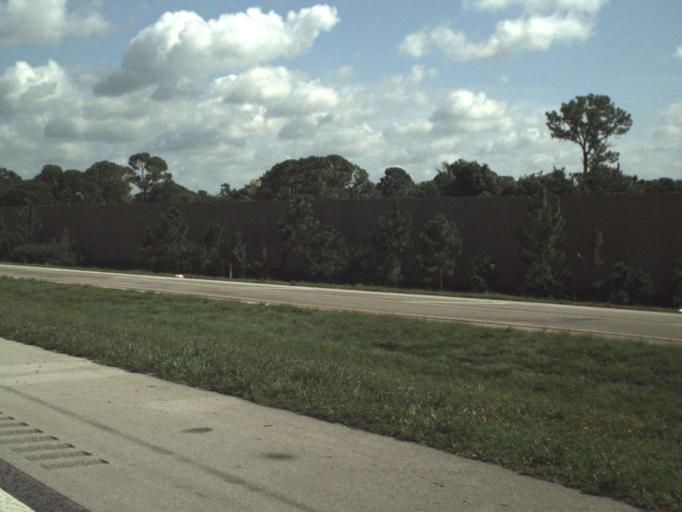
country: US
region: Florida
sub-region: Palm Beach County
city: Limestone Creek
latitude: 26.8866
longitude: -80.1302
